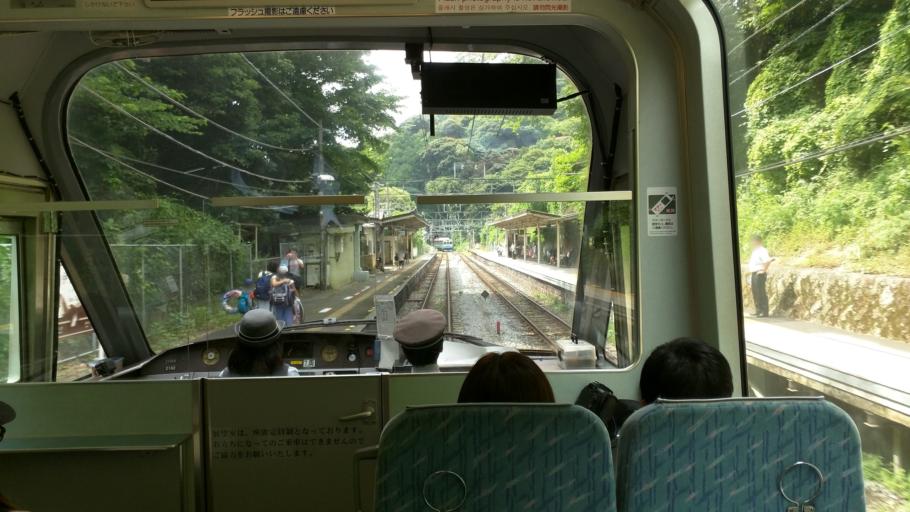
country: JP
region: Shizuoka
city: Atami
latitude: 35.0627
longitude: 139.0667
